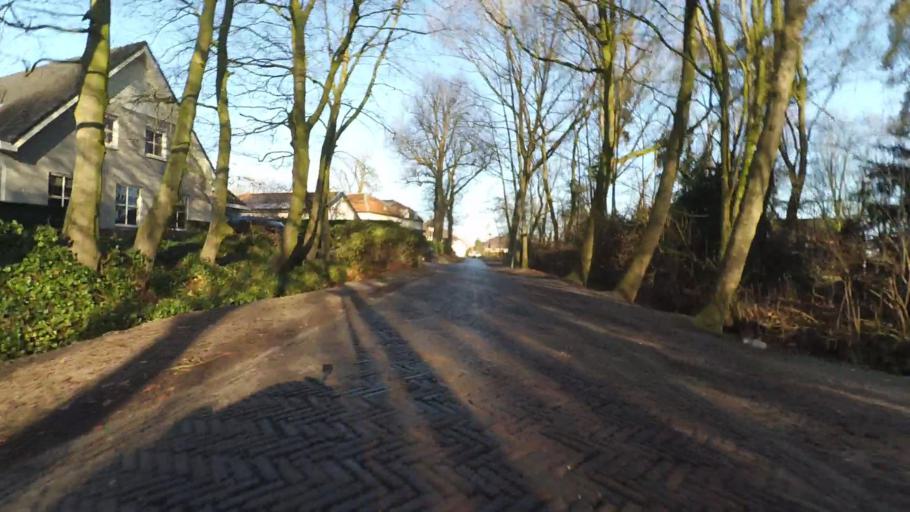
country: NL
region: Gelderland
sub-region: Gemeente Nijkerk
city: Nijkerk
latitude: 52.2196
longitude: 5.4675
